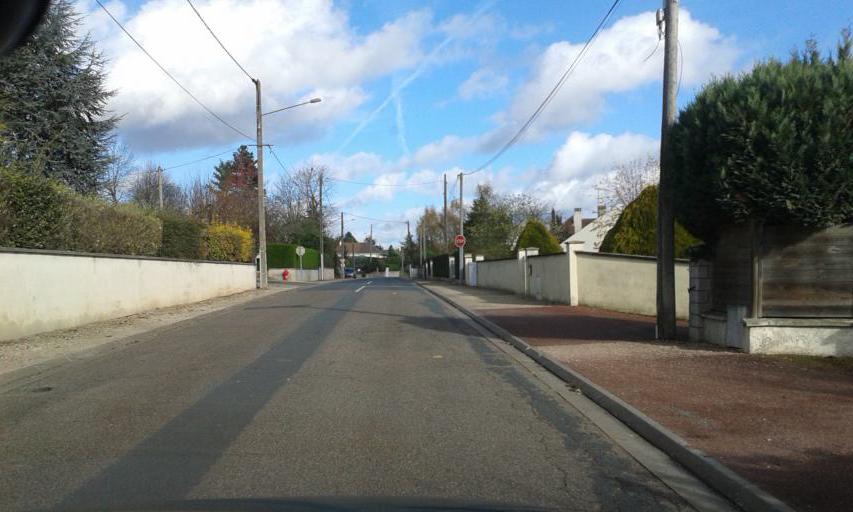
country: FR
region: Centre
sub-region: Departement du Loiret
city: Tavers
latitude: 47.7639
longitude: 1.6237
